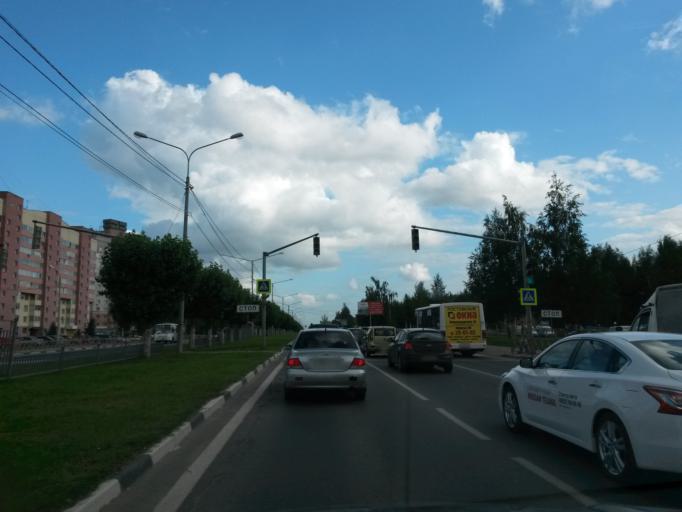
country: RU
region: Jaroslavl
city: Yaroslavl
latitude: 57.5840
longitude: 39.9077
